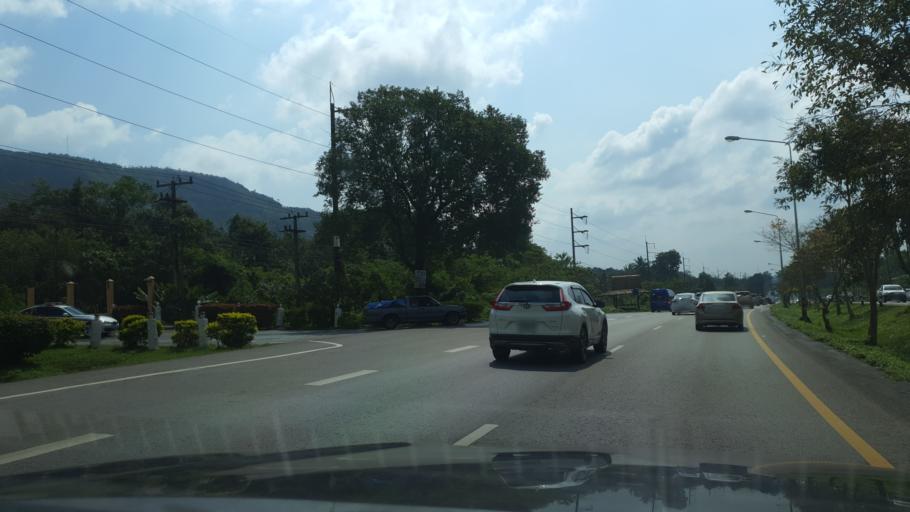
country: TH
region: Chumphon
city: Tha Sae
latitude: 10.5804
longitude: 99.1151
